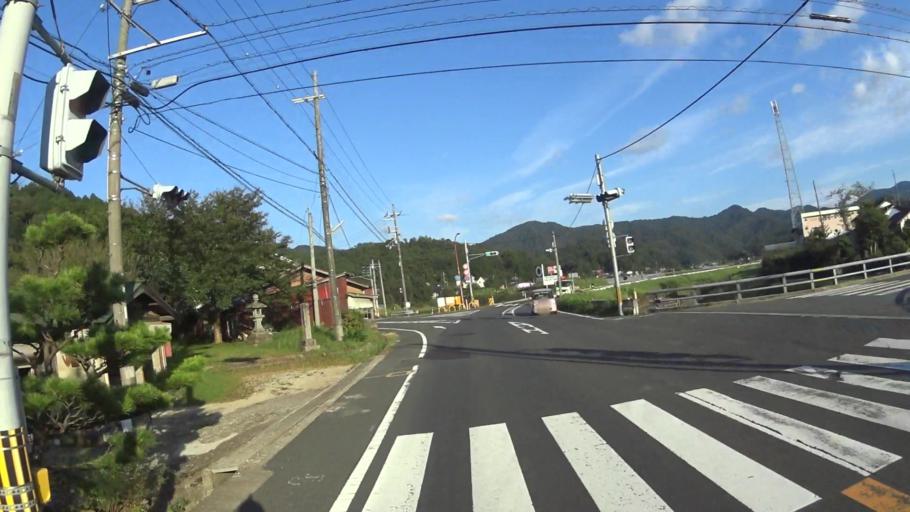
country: JP
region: Hyogo
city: Toyooka
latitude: 35.5790
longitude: 134.9719
